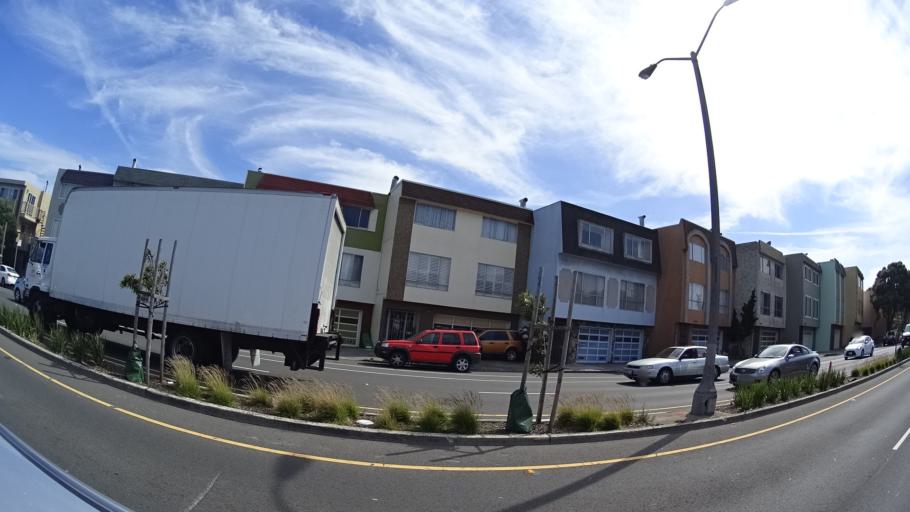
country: US
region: California
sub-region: San Mateo County
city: Daly City
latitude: 37.7145
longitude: -122.4478
